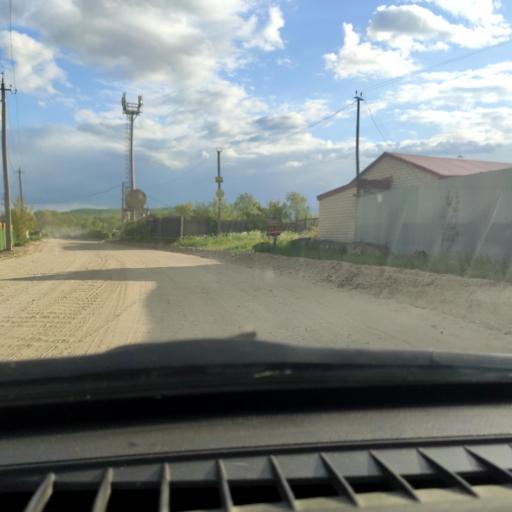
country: RU
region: Samara
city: Zhigulevsk
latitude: 53.4564
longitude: 49.5362
